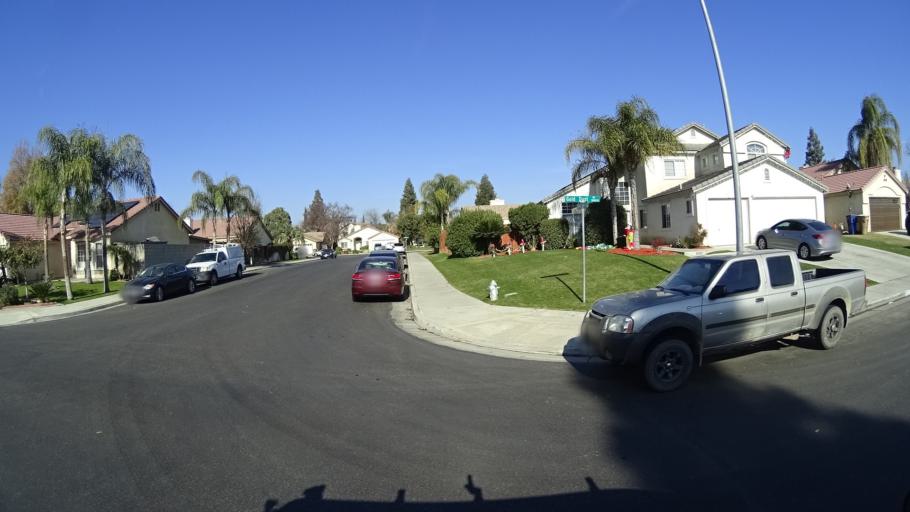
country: US
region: California
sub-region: Kern County
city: Greenacres
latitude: 35.3195
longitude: -119.1125
